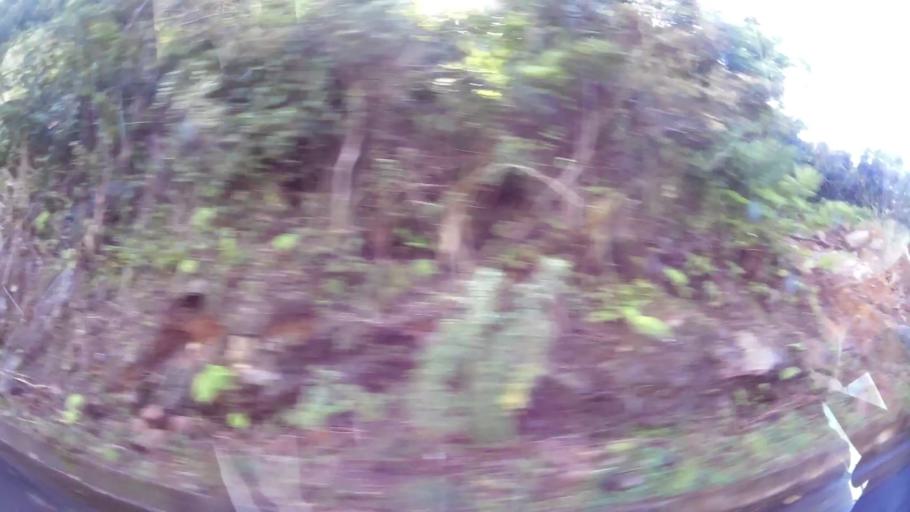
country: DM
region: Saint Paul
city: Pont Casse
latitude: 15.3719
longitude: -61.3483
